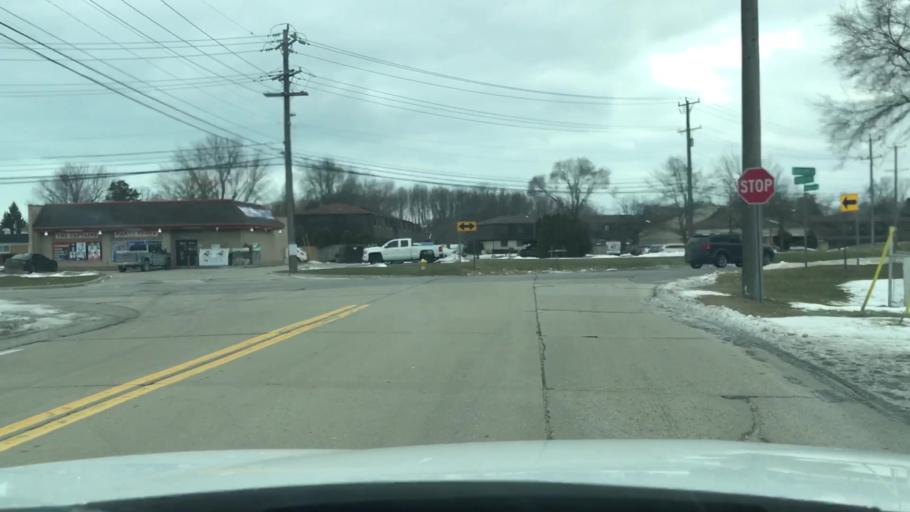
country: US
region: Michigan
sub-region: Macomb County
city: Mount Clemens
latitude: 42.5931
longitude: -82.8540
